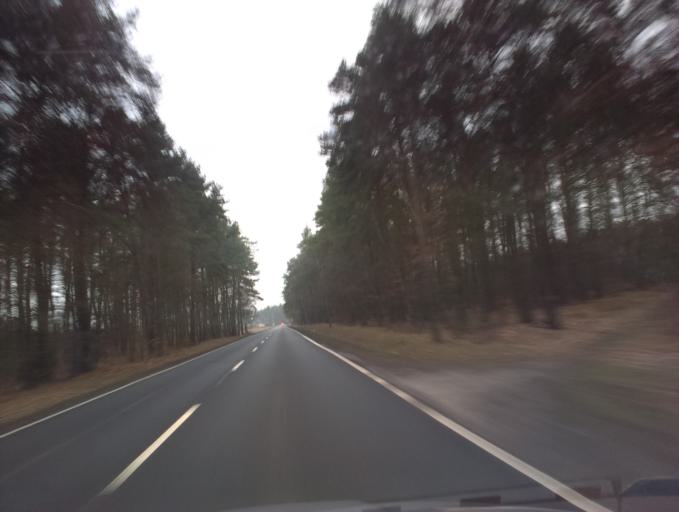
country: PL
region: Greater Poland Voivodeship
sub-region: Powiat zlotowski
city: Jastrowie
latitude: 53.3918
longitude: 16.7871
